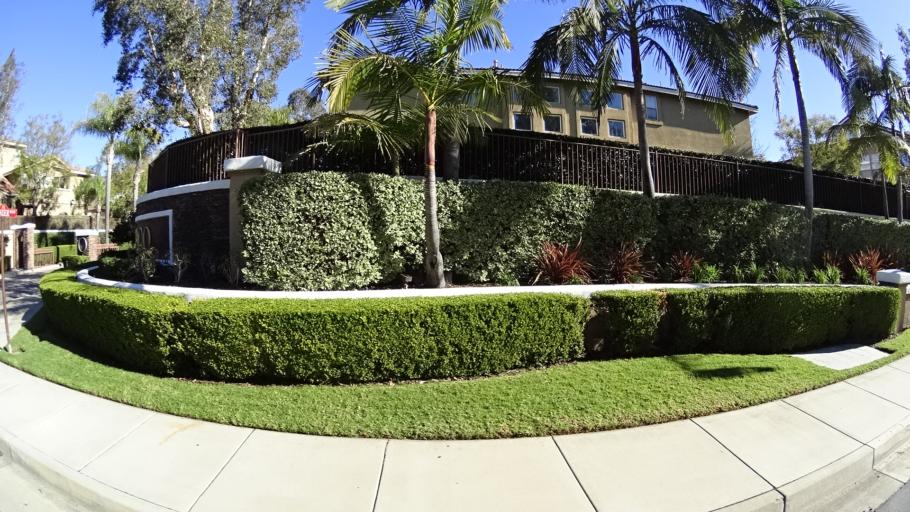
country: US
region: California
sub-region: Orange County
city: Villa Park
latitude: 33.8507
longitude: -117.7417
